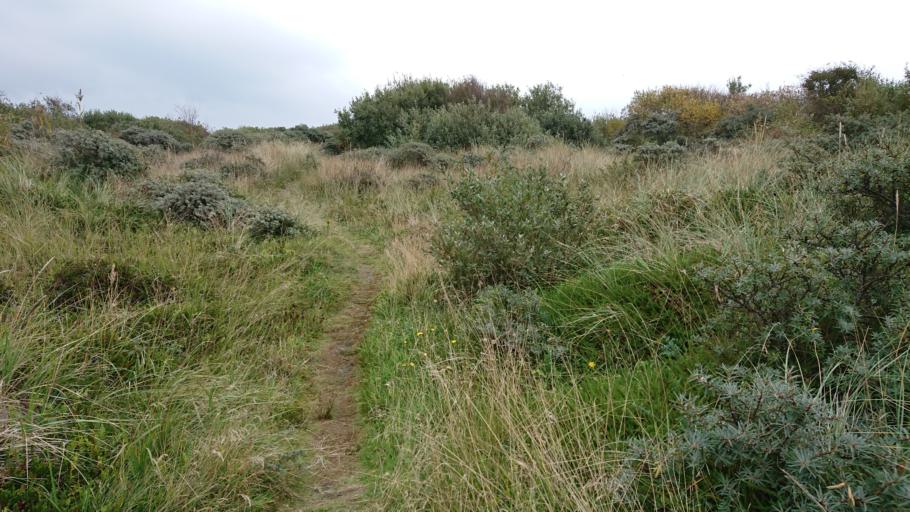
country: DK
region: North Denmark
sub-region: Frederikshavn Kommune
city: Skagen
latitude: 57.7483
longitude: 10.6183
